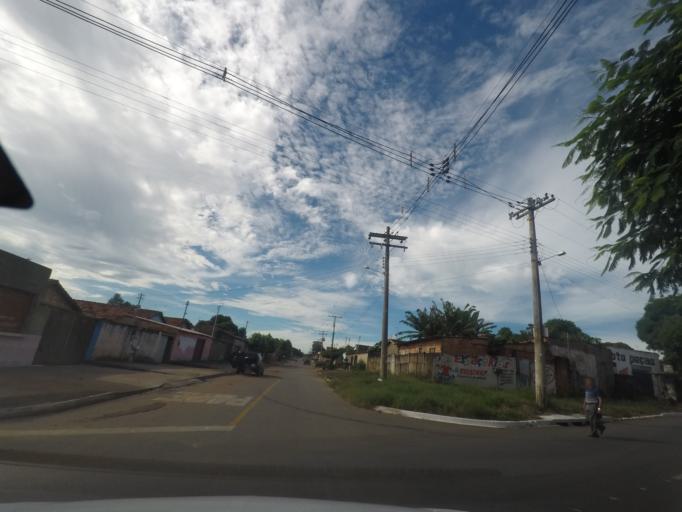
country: BR
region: Goias
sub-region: Aparecida De Goiania
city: Aparecida de Goiania
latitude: -16.8191
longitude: -49.3058
